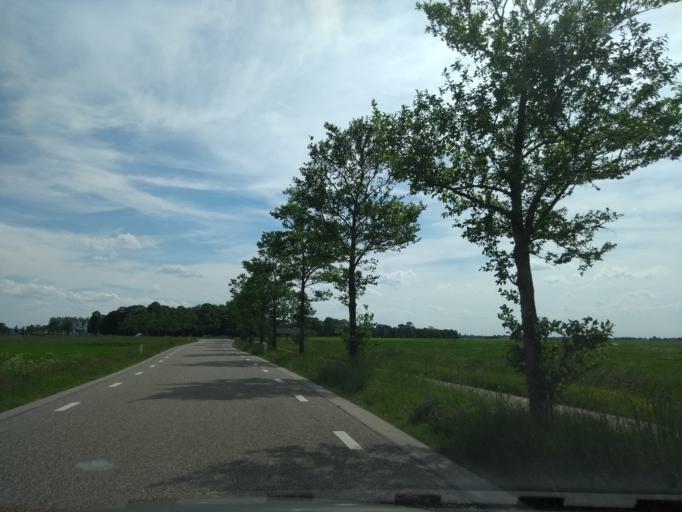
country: NL
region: Groningen
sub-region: Gemeente Zuidhorn
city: Oldehove
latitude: 53.2826
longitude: 6.4233
